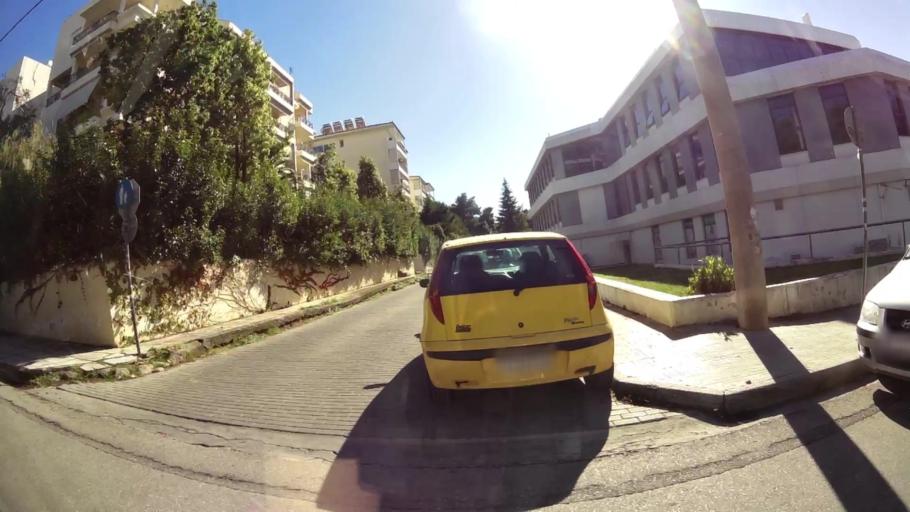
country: GR
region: Attica
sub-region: Nomarchia Athinas
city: Nea Erythraia
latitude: 38.0934
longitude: 23.8099
